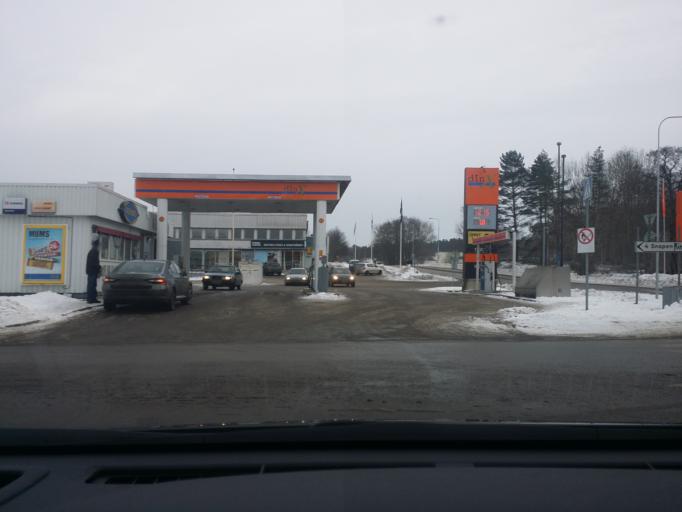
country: SE
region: Vaestra Goetaland
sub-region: Mariestads Kommun
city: Mariestad
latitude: 58.7102
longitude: 13.8357
